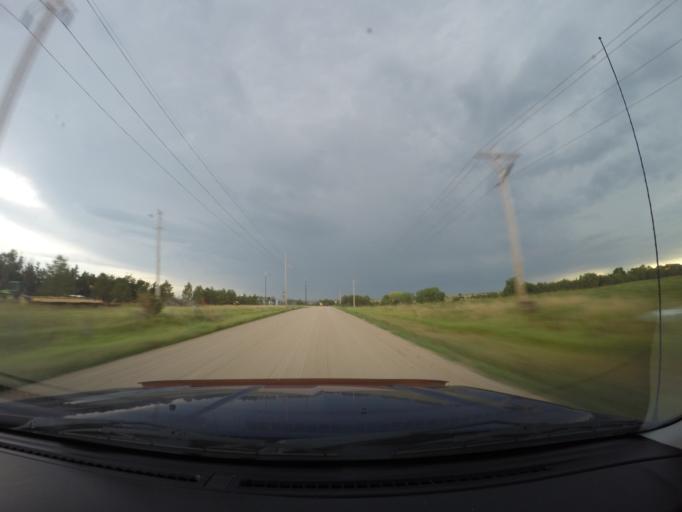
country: US
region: Nebraska
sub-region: Buffalo County
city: Kearney
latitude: 40.8441
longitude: -99.2531
